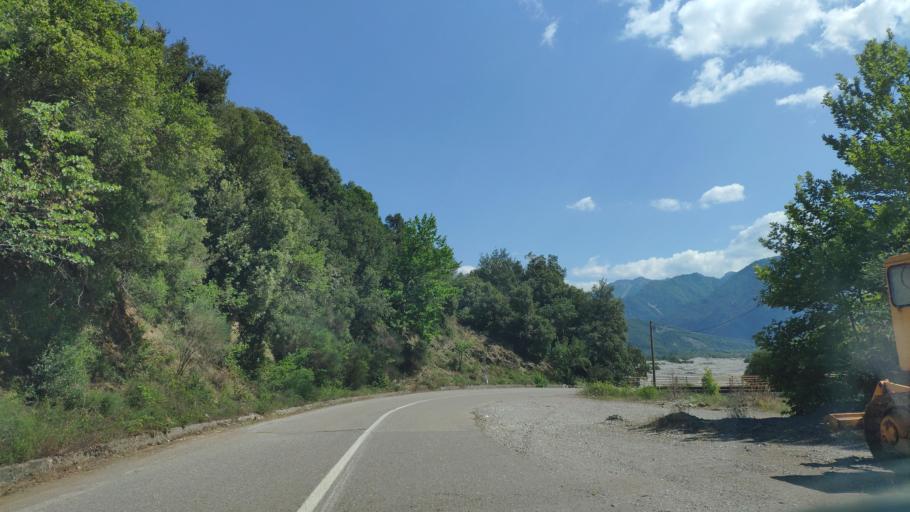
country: GR
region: Central Greece
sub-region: Nomos Evrytanias
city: Kerasochori
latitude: 38.9986
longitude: 21.5711
